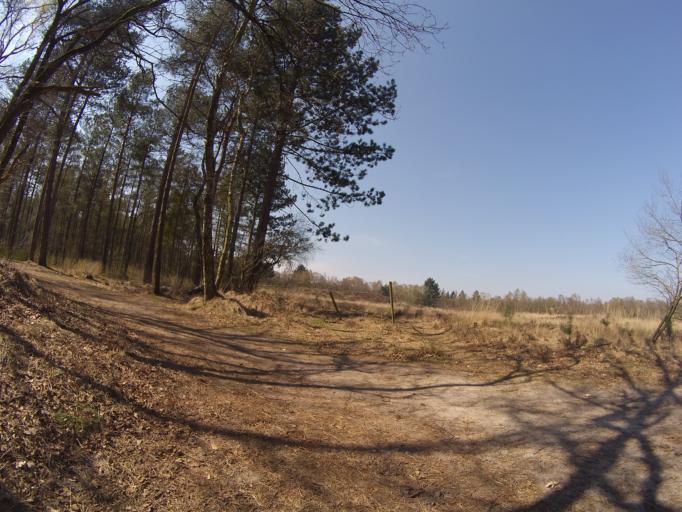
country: NL
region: Utrecht
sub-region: Gemeente Utrechtse Heuvelrug
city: Overberg
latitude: 52.0199
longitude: 5.5099
